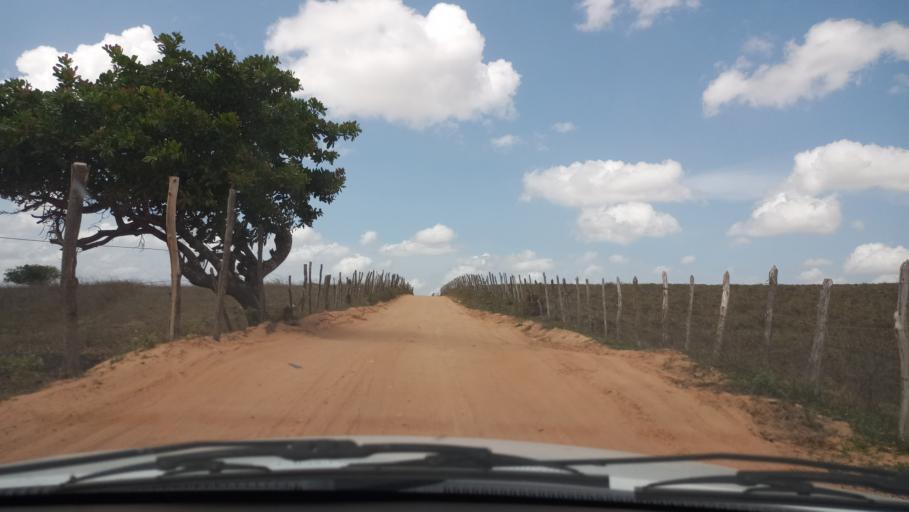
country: BR
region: Rio Grande do Norte
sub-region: Montanhas
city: Montanhas
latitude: -6.3550
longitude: -35.3356
